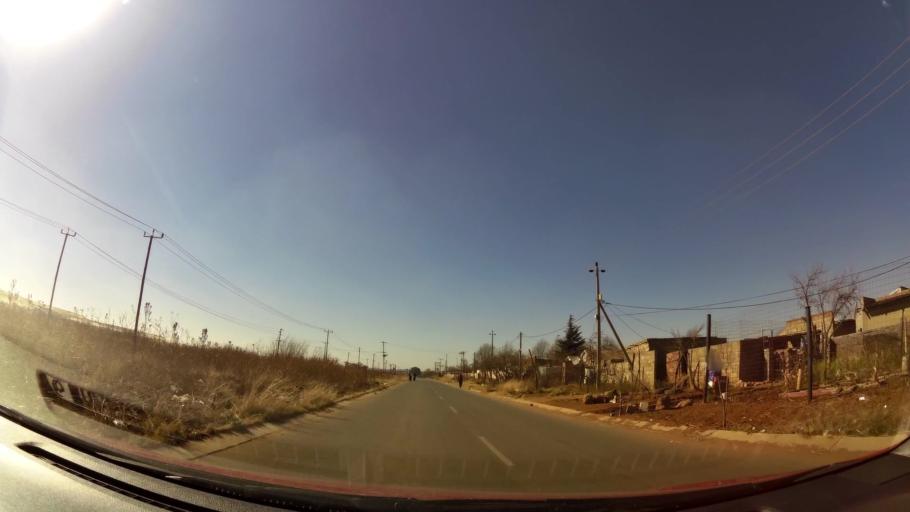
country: ZA
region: Gauteng
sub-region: City of Johannesburg Metropolitan Municipality
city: Soweto
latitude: -26.2155
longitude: 27.8312
